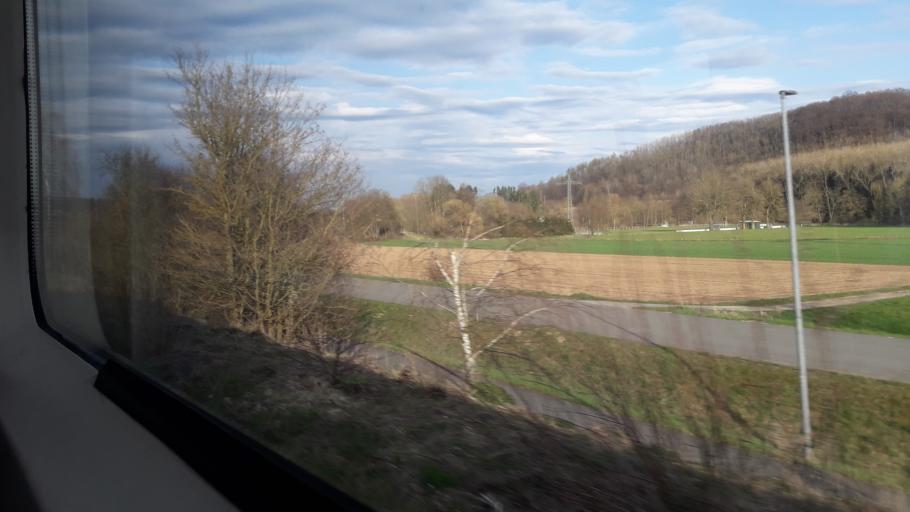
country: DE
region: North Rhine-Westphalia
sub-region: Regierungsbezirk Detmold
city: Willebadessen
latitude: 51.5205
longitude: 9.0154
